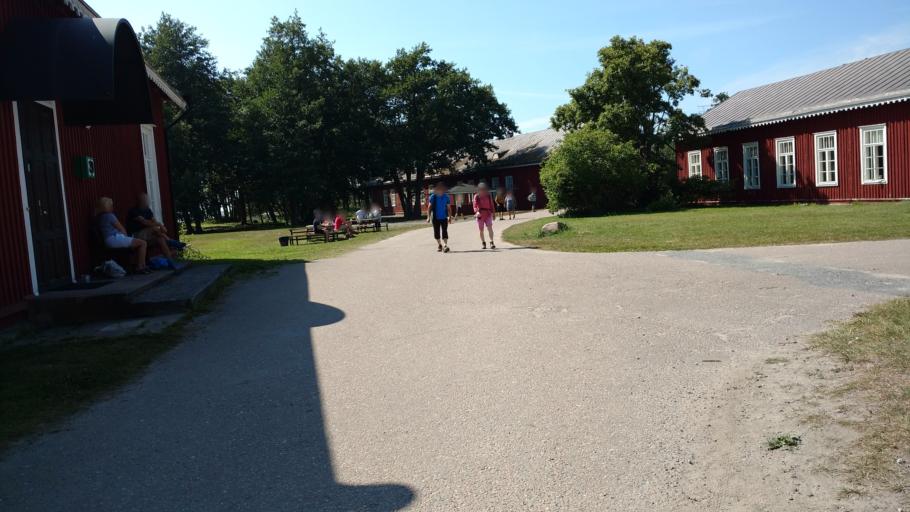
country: FI
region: Varsinais-Suomi
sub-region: Aboland-Turunmaa
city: Dragsfjaerd
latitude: 59.8071
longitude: 22.3368
